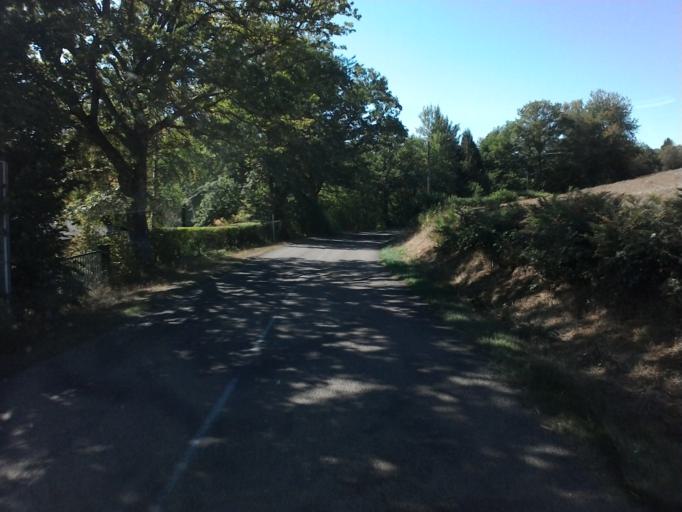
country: FR
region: Bourgogne
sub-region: Departement de la Nievre
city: Lormes
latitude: 47.2822
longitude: 3.9953
